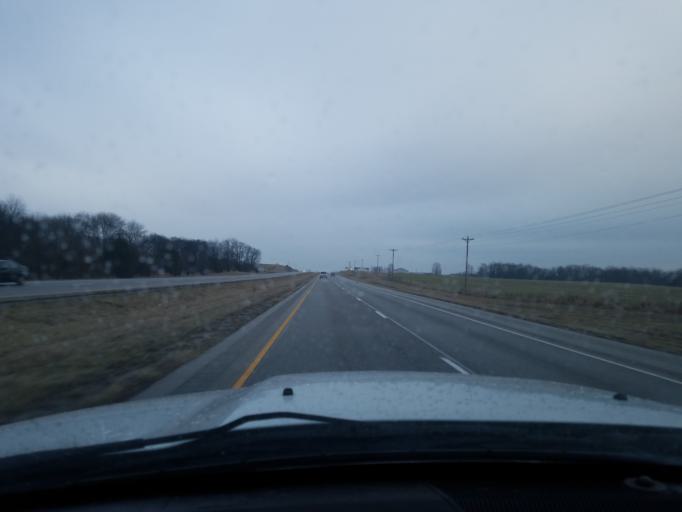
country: US
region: Kentucky
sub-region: Logan County
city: Auburn
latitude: 36.8703
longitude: -86.7039
